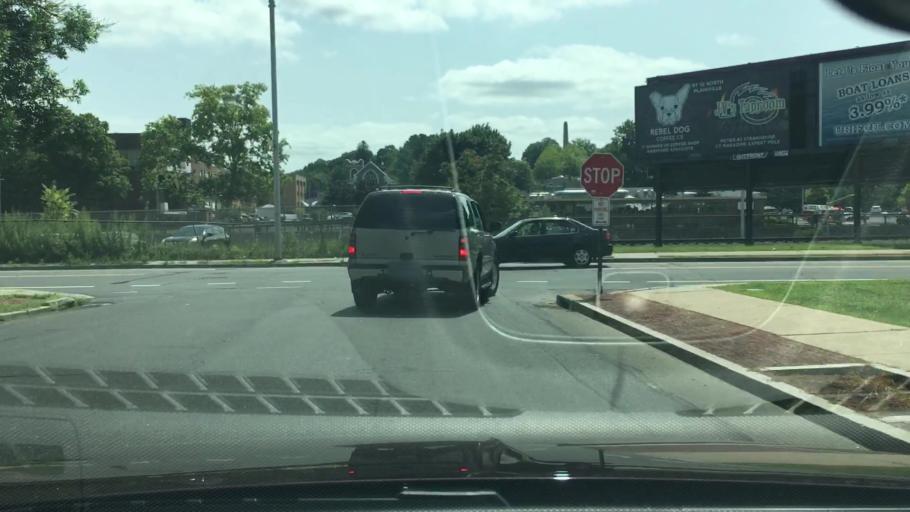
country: US
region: Connecticut
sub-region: Hartford County
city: New Britain
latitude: 41.6701
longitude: -72.7869
